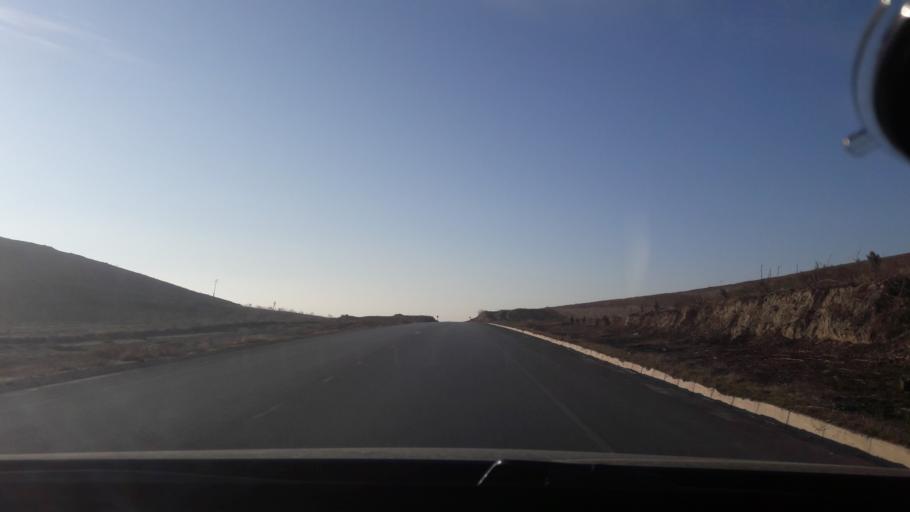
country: TJ
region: Khatlon
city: Danghara
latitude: 38.2153
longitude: 69.2786
